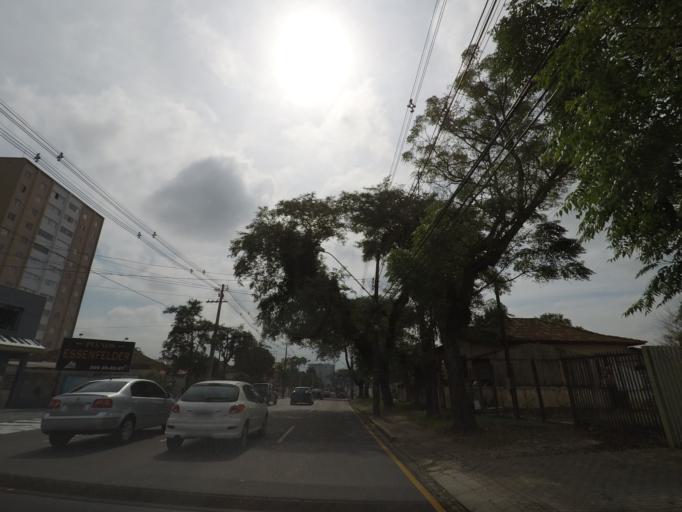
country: BR
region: Parana
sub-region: Curitiba
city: Curitiba
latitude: -25.4903
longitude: -49.2916
